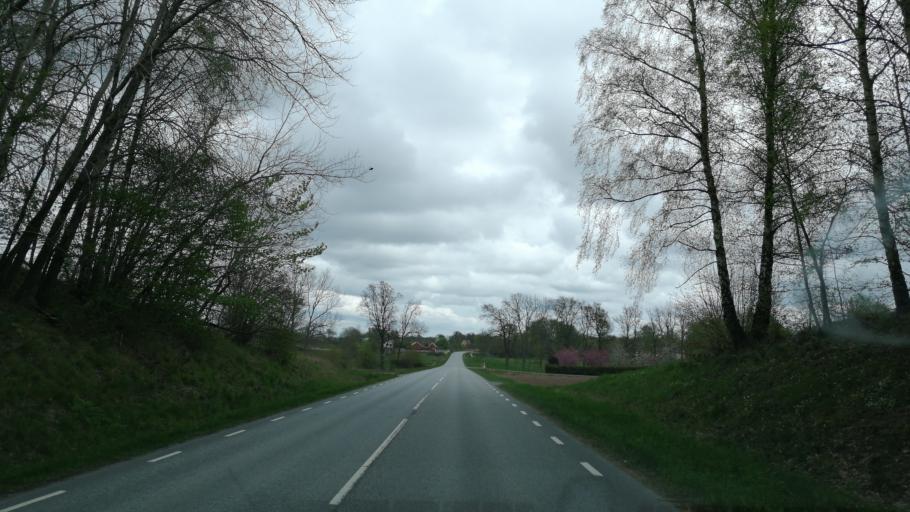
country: SE
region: Skane
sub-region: Kristianstads Kommun
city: Onnestad
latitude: 55.9945
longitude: 14.0497
